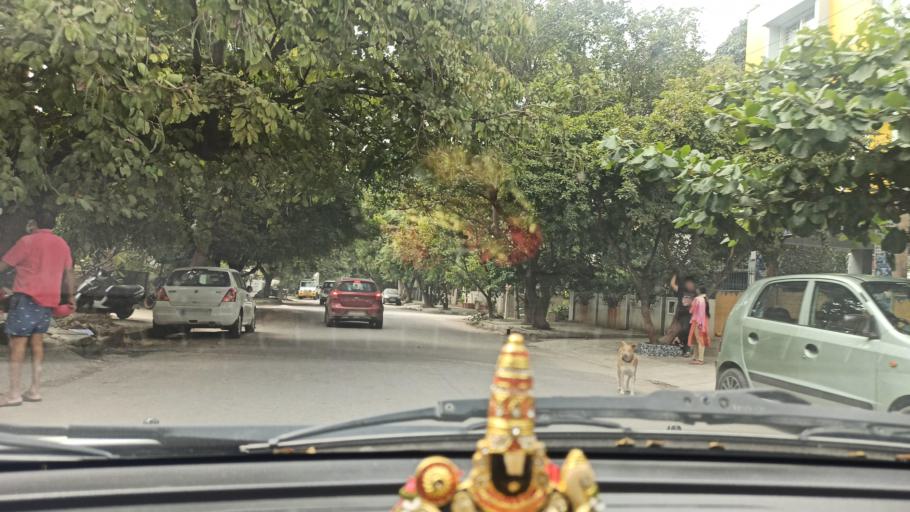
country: IN
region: Karnataka
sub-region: Bangalore Urban
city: Bangalore
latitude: 13.0185
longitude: 77.6499
